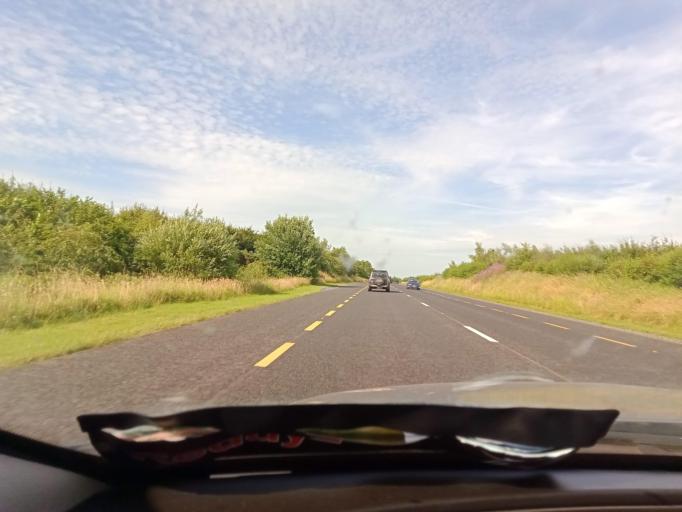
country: IE
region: Leinster
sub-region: An Iarmhi
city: An Muileann gCearr
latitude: 53.4838
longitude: -7.3457
